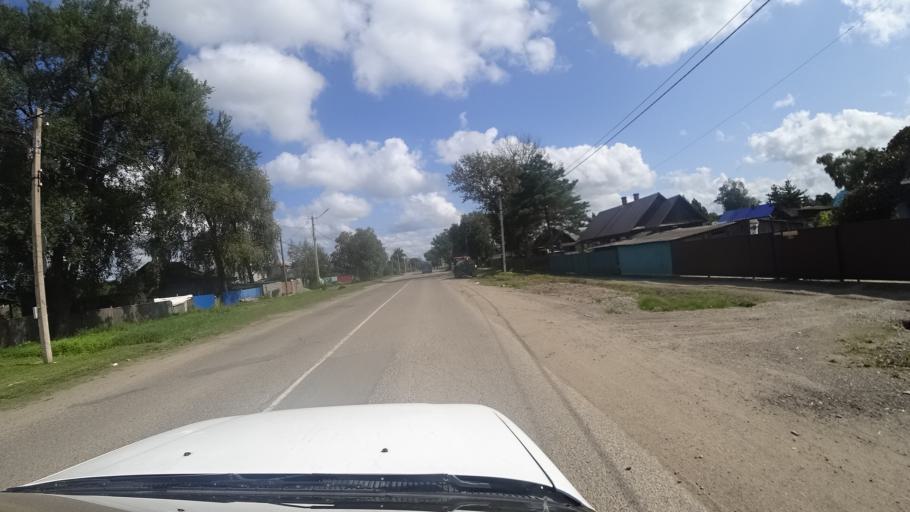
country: RU
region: Primorskiy
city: Dal'nerechensk
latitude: 45.9318
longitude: 133.7581
